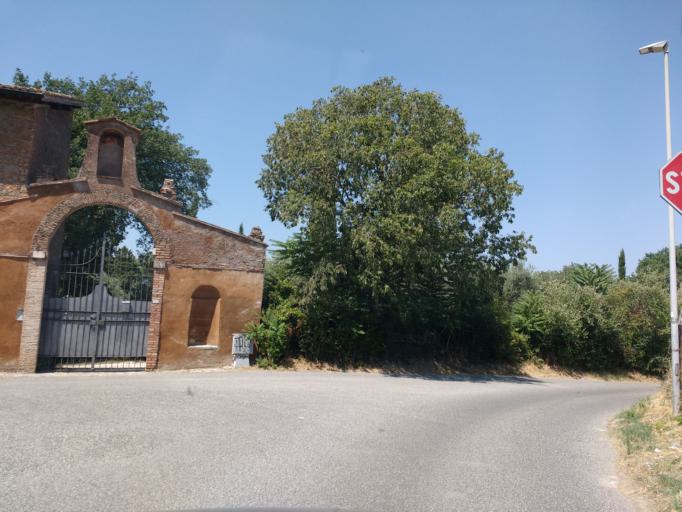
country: IT
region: Latium
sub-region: Citta metropolitana di Roma Capitale
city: Villa Adriana
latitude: 41.9478
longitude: 12.7811
